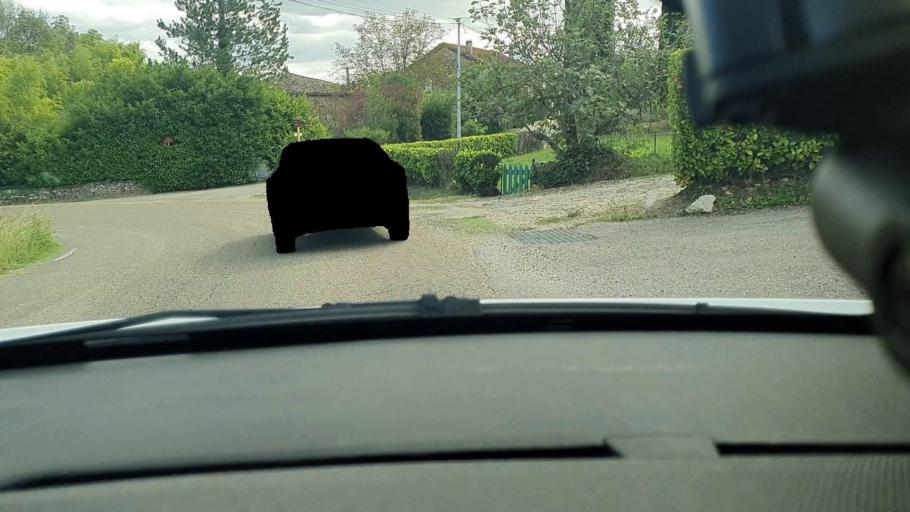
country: FR
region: Languedoc-Roussillon
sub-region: Departement du Gard
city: Les Mages
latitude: 44.2127
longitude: 4.1940
